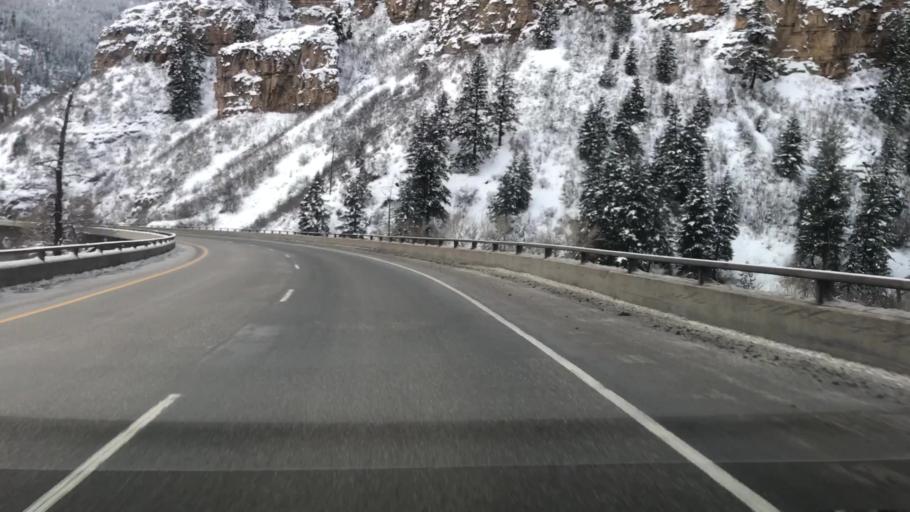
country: US
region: Colorado
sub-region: Garfield County
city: Glenwood Springs
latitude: 39.6082
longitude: -107.1552
